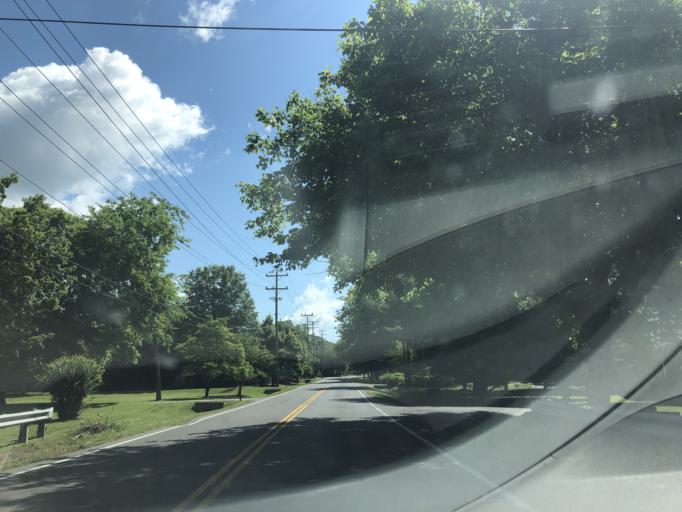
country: US
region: Tennessee
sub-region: Davidson County
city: Belle Meade
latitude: 36.0718
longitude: -86.9286
